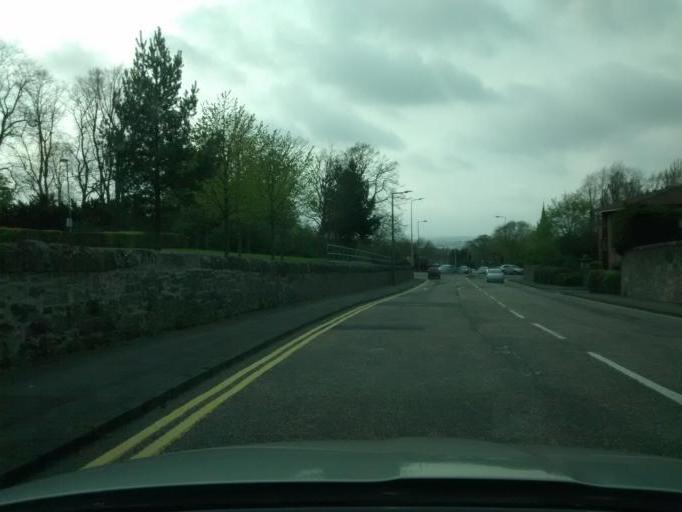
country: GB
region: Scotland
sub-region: Edinburgh
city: Colinton
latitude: 55.9195
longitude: -3.2386
